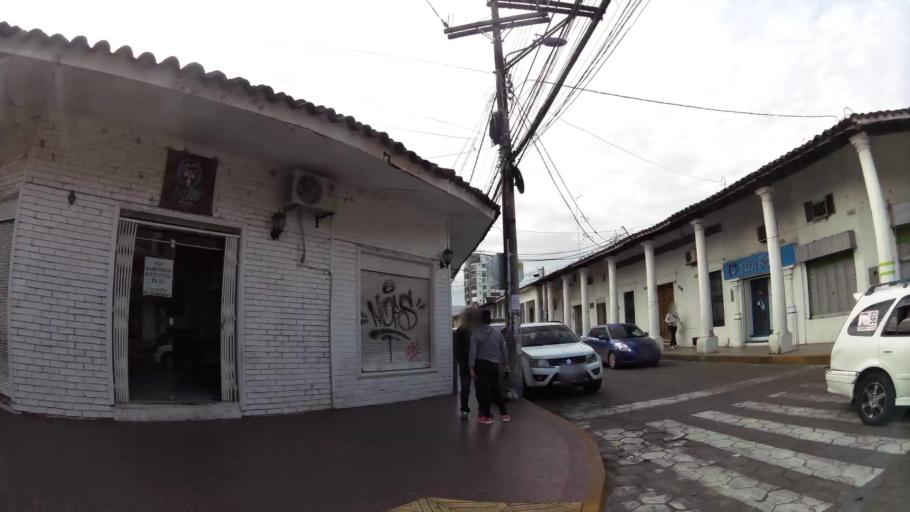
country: BO
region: Santa Cruz
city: Santa Cruz de la Sierra
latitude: -17.7816
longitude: -63.1807
